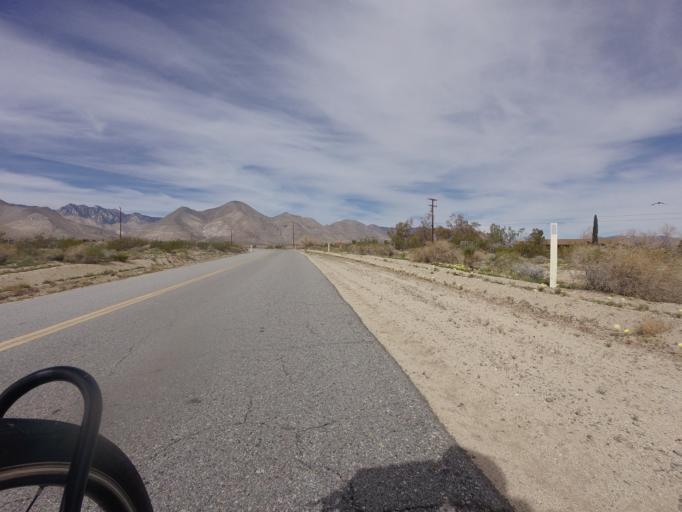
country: US
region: California
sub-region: Kern County
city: Inyokern
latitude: 35.7759
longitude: -117.8516
